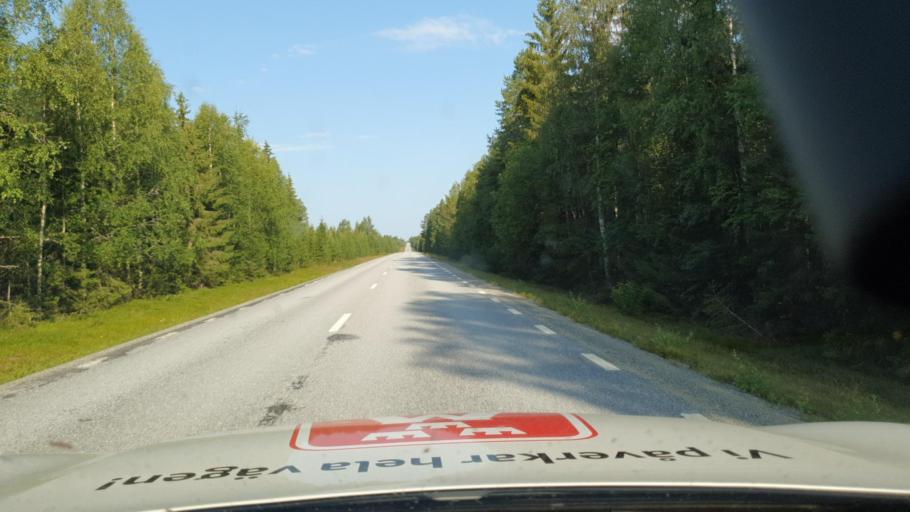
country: SE
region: Vaesterbotten
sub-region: Bjurholms Kommun
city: Bjurholm
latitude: 63.9416
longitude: 18.9255
